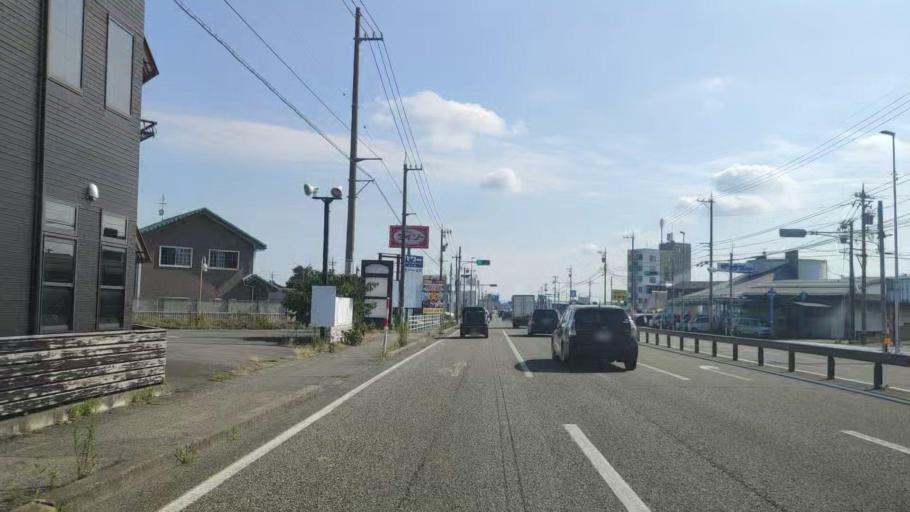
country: JP
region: Ishikawa
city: Matsuto
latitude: 36.5202
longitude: 136.5792
